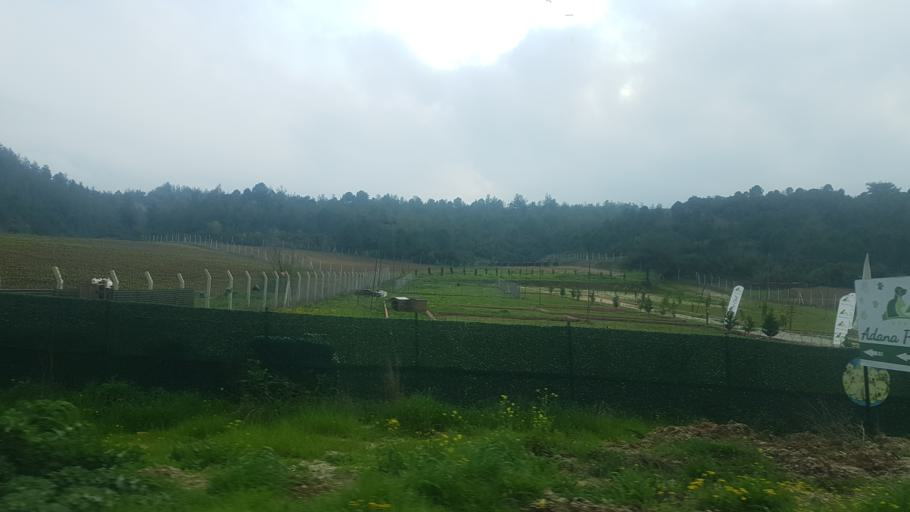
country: TR
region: Mersin
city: Yenice
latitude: 37.0915
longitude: 35.1490
